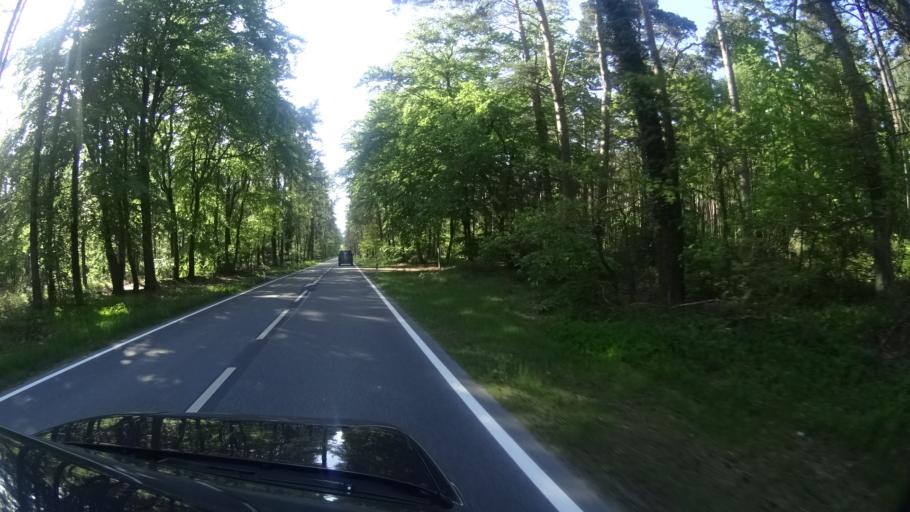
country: DE
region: Mecklenburg-Vorpommern
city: Born
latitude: 54.3910
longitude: 12.5239
